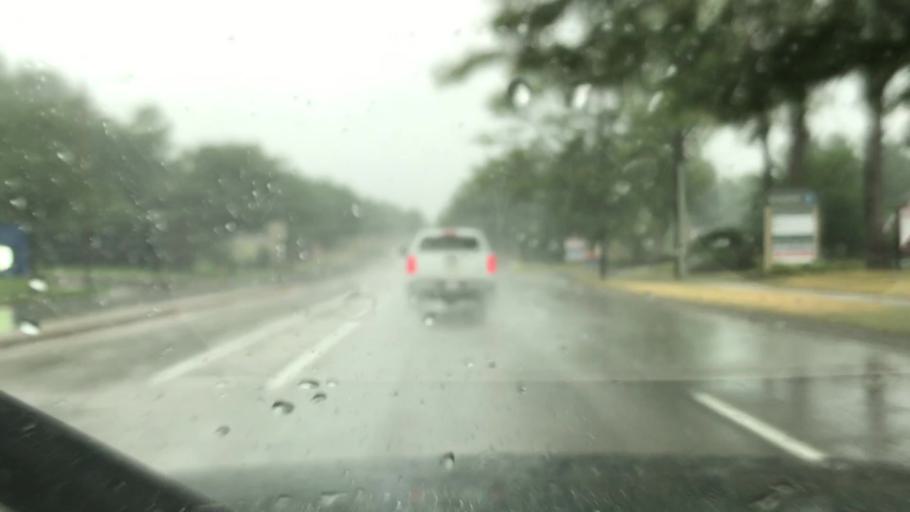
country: US
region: Michigan
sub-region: Kent County
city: Wyoming
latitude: 42.8838
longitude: -85.7242
